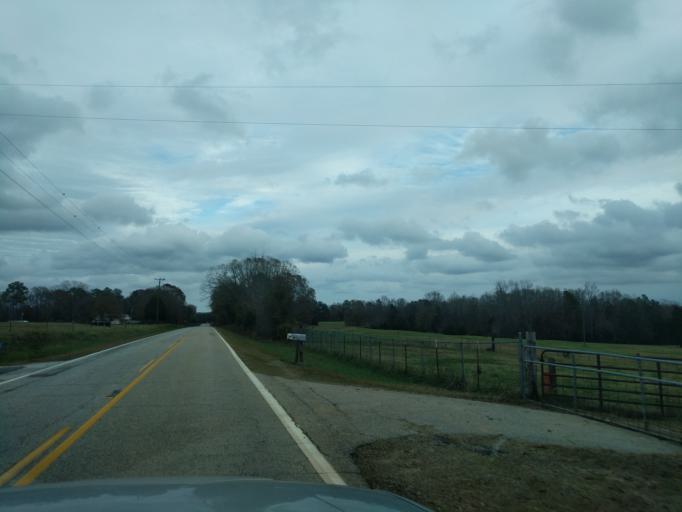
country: US
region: South Carolina
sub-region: Greenwood County
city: Ware Shoals
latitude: 34.4070
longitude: -82.1291
